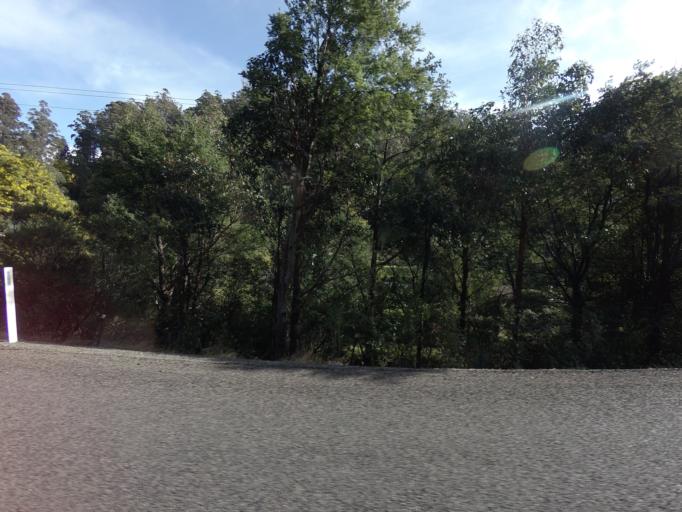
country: AU
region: Tasmania
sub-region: Huon Valley
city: Huonville
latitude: -43.0405
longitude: 147.1333
